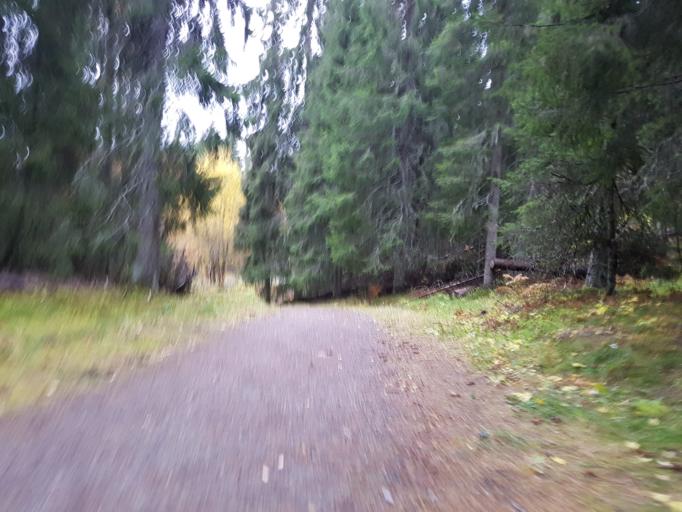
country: NO
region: Sor-Trondelag
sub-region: Trondheim
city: Trondheim
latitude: 63.3806
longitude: 10.3315
